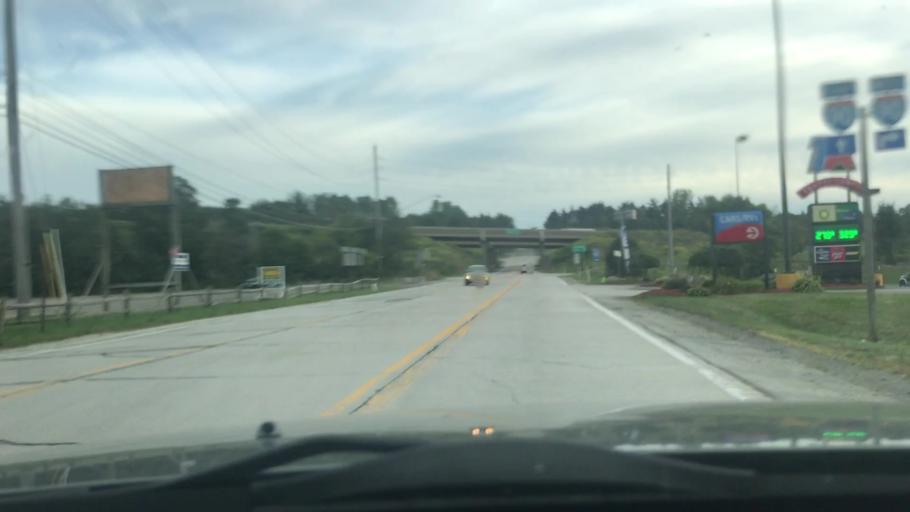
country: US
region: Pennsylvania
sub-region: Erie County
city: Northwest Harborcreek
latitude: 42.1415
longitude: -79.9234
